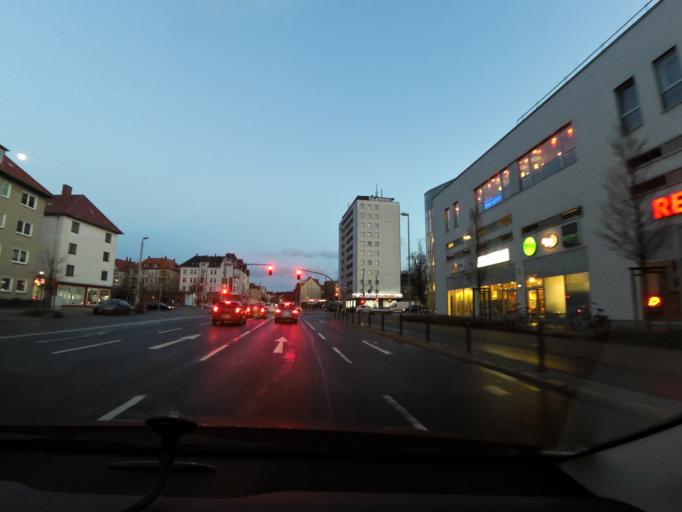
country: DE
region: Lower Saxony
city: Braunschweig
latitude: 52.2730
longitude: 10.5063
